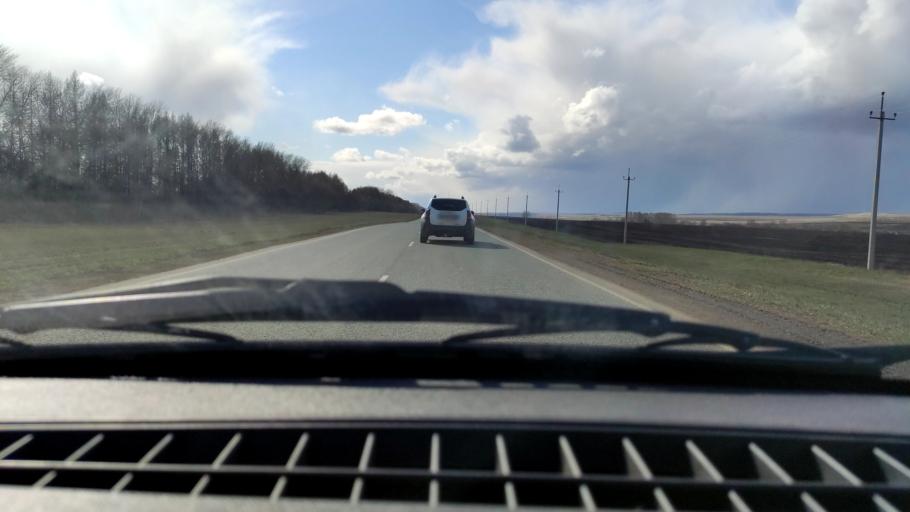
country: RU
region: Bashkortostan
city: Chekmagush
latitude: 55.1107
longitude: 54.9244
